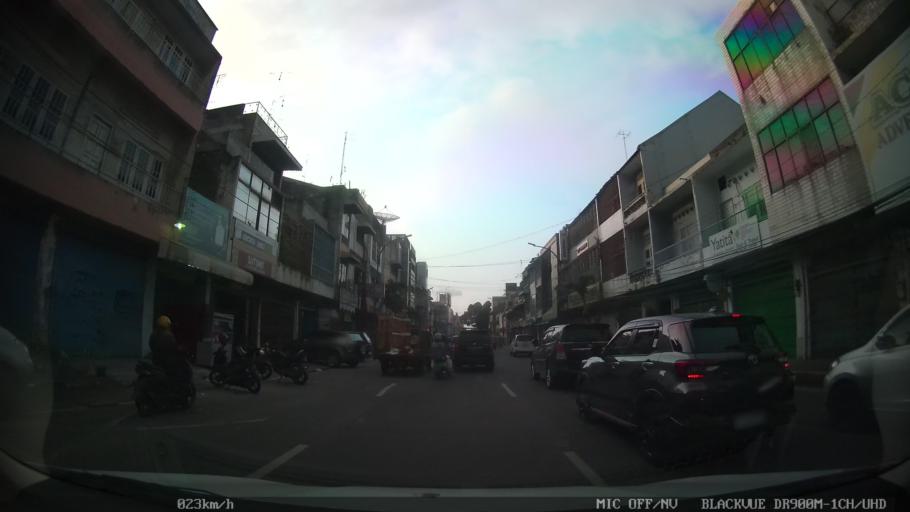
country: ID
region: North Sumatra
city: Medan
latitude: 3.5857
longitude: 98.6863
